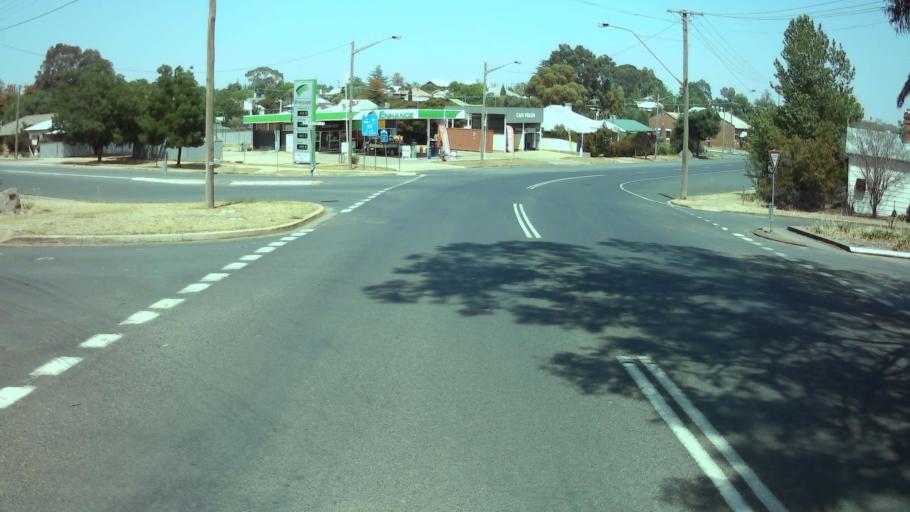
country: AU
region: New South Wales
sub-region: Weddin
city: Grenfell
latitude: -33.8954
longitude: 148.1660
